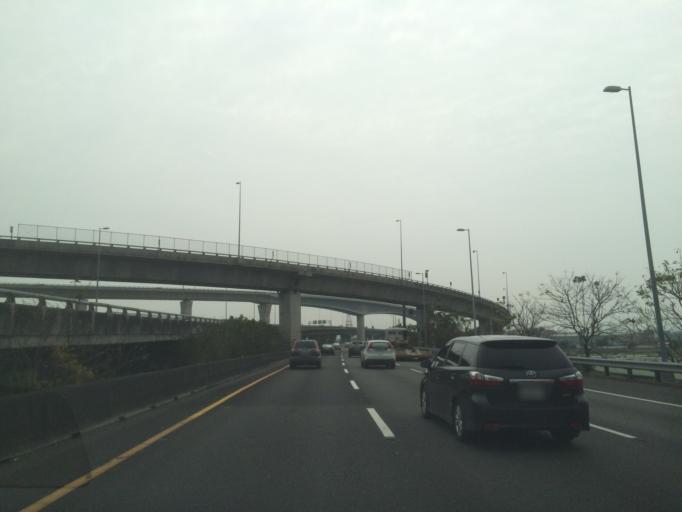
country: TW
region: Taiwan
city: Zhongxing New Village
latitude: 24.0519
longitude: 120.6782
